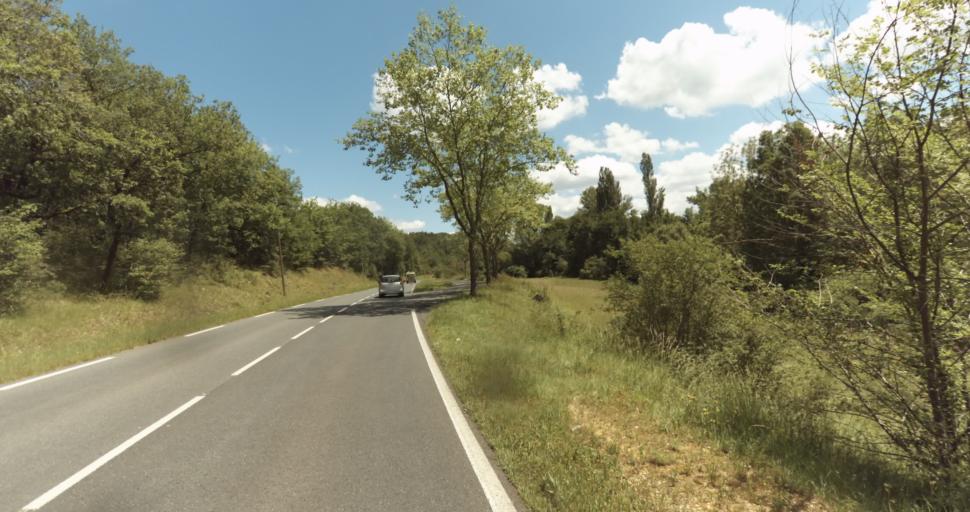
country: FR
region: Aquitaine
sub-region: Departement de la Dordogne
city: Le Bugue
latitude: 44.8455
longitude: 0.8471
